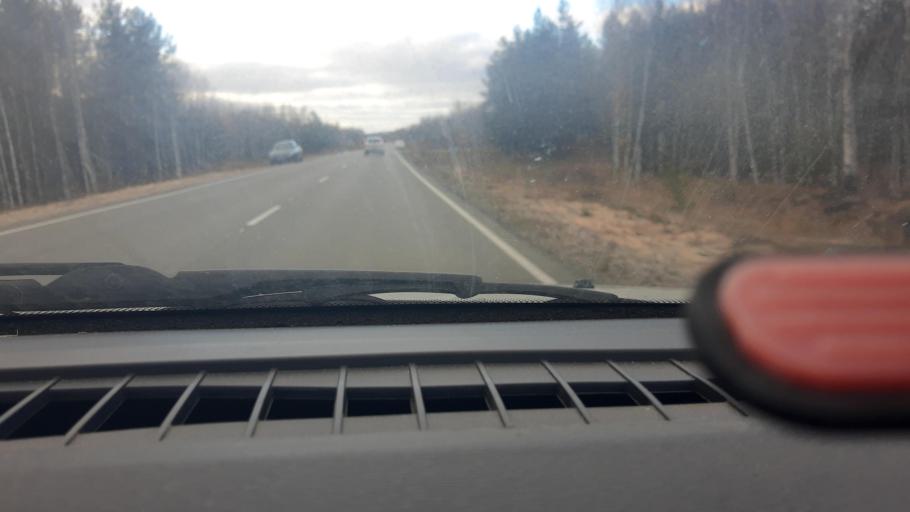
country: RU
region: Nizjnij Novgorod
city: Babino
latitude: 56.2961
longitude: 43.6317
